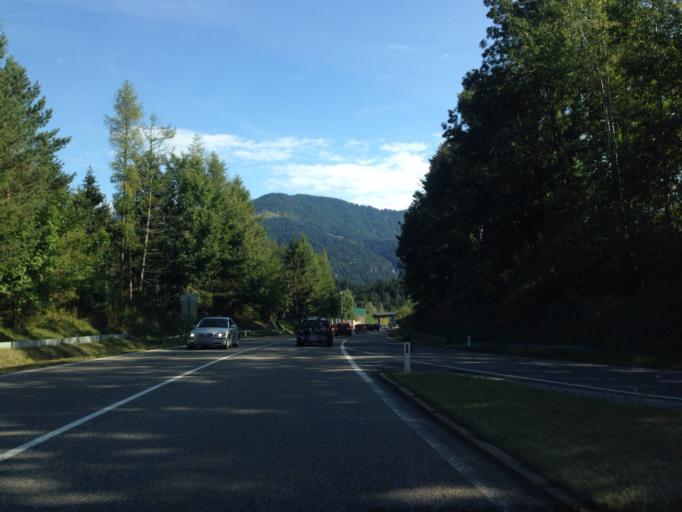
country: AT
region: Tyrol
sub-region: Politischer Bezirk Reutte
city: Breitenwang
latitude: 47.4810
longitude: 10.7353
